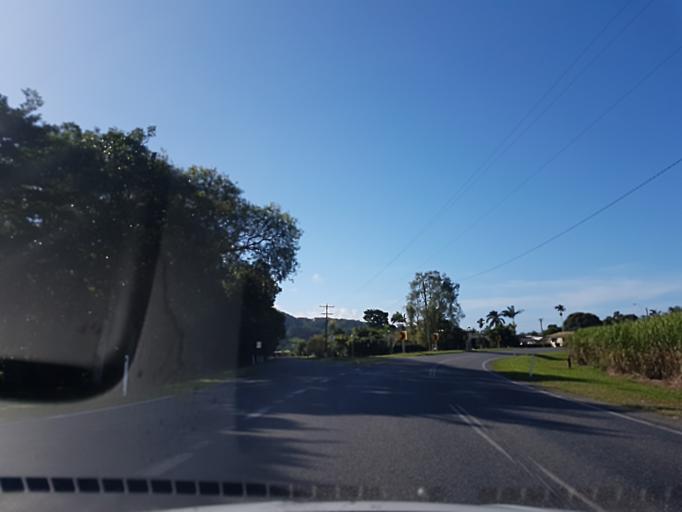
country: AU
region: Queensland
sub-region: Cairns
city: Port Douglas
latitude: -16.4420
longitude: 145.3729
